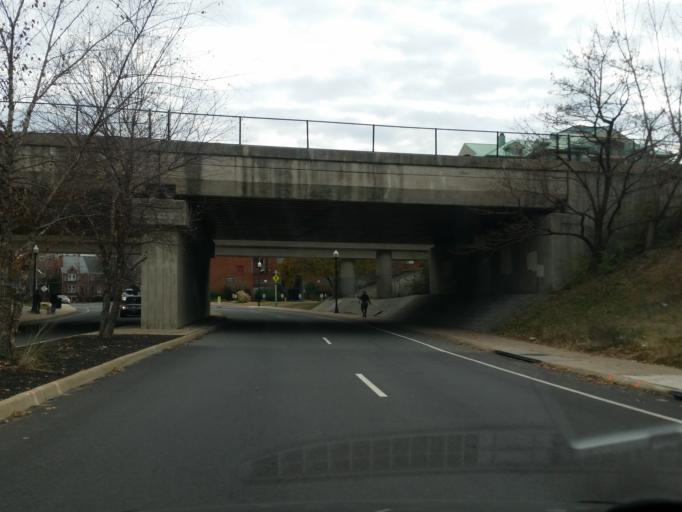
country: US
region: Virginia
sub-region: City of Alexandria
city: Alexandria
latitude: 38.8131
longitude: -77.0553
